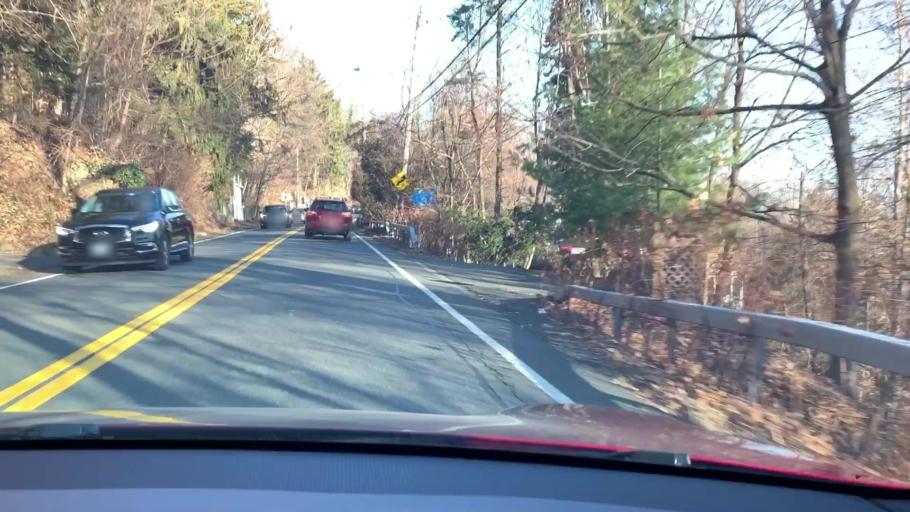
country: US
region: New York
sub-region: Rockland County
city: Piermont
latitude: 41.0503
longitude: -73.9224
